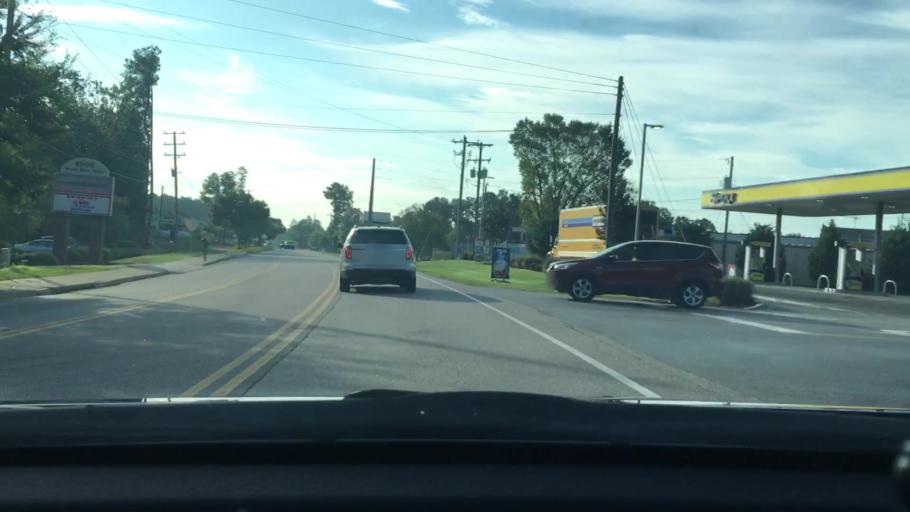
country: US
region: South Carolina
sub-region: Lexington County
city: Irmo
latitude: 34.1076
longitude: -81.1900
